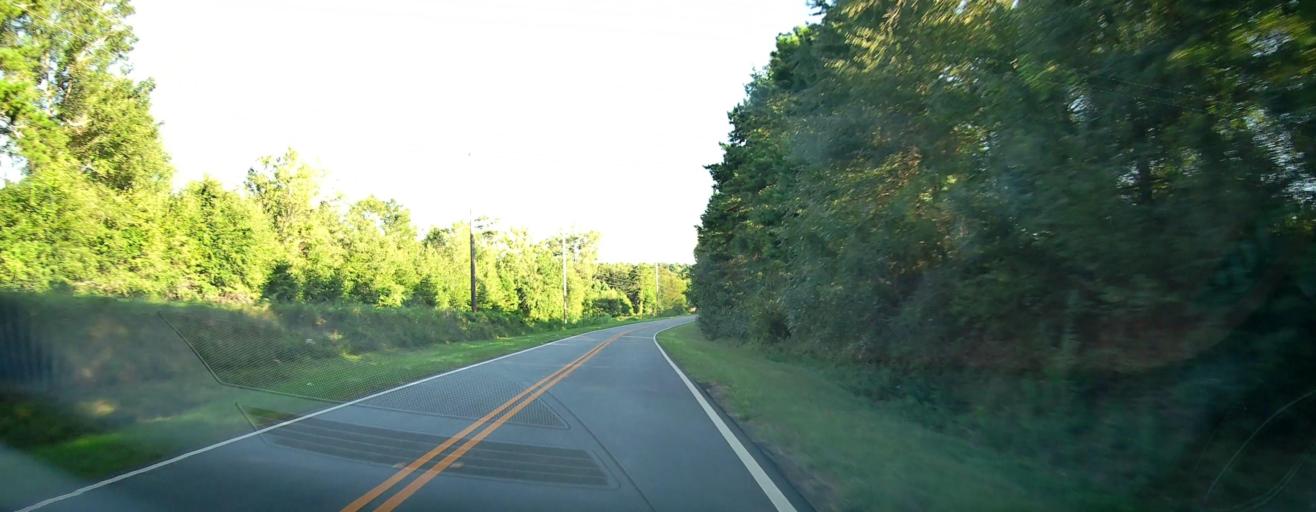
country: US
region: Georgia
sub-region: Pulaski County
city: Hawkinsville
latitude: 32.3040
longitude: -83.4503
